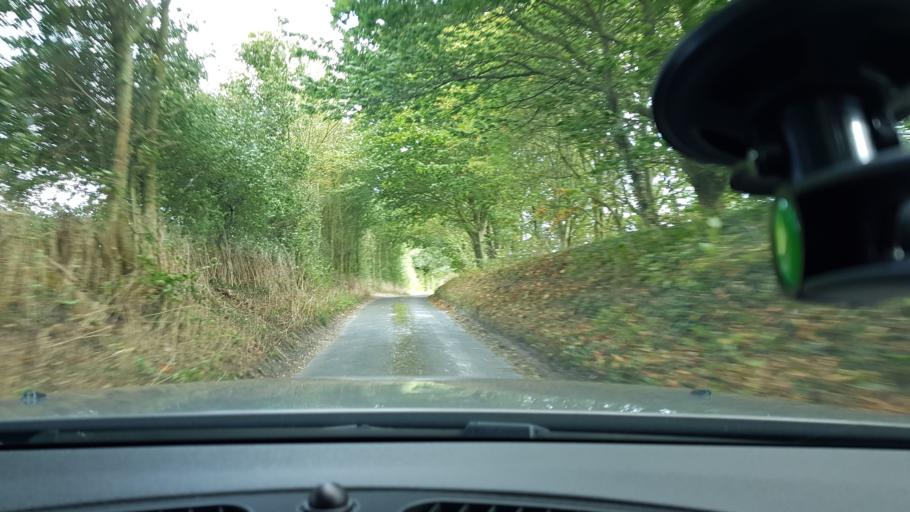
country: GB
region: England
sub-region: West Berkshire
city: Hungerford
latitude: 51.4263
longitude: -1.5082
